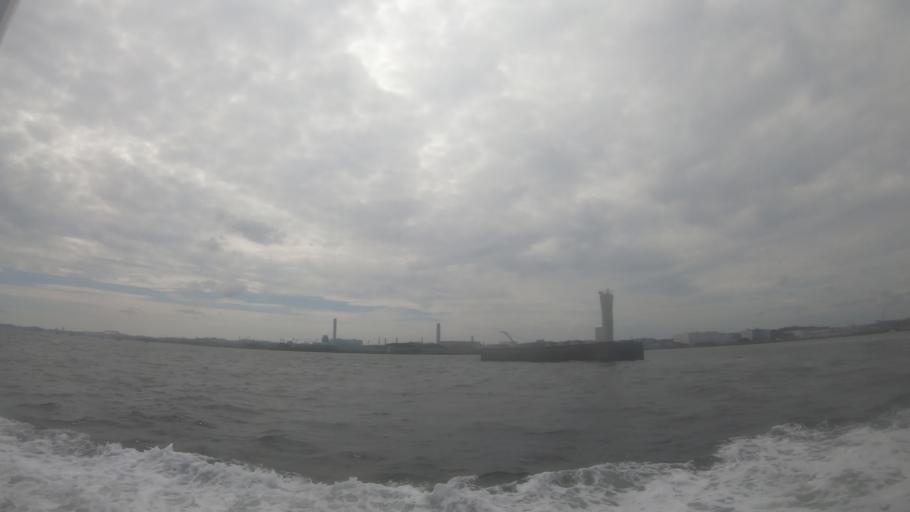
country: JP
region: Kanagawa
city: Yokohama
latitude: 35.3790
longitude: 139.6590
